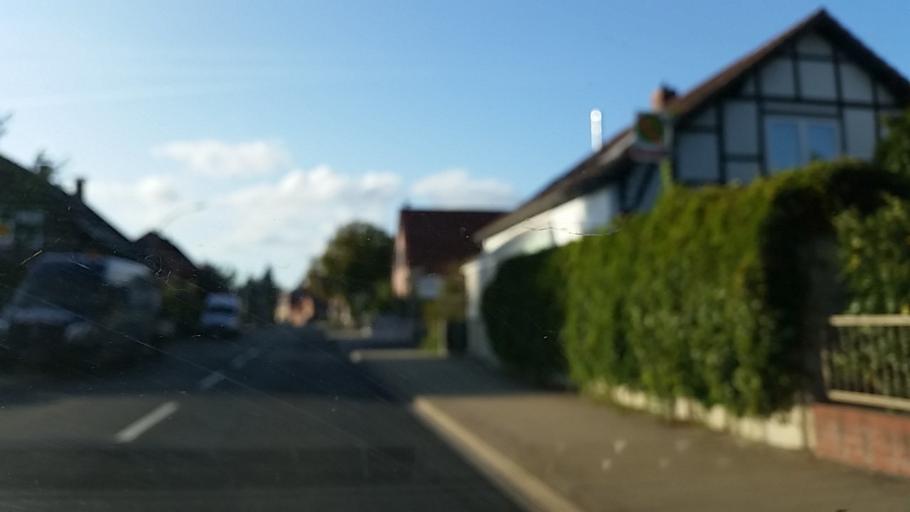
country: DE
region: Lower Saxony
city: Vordorf
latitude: 52.3164
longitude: 10.5305
